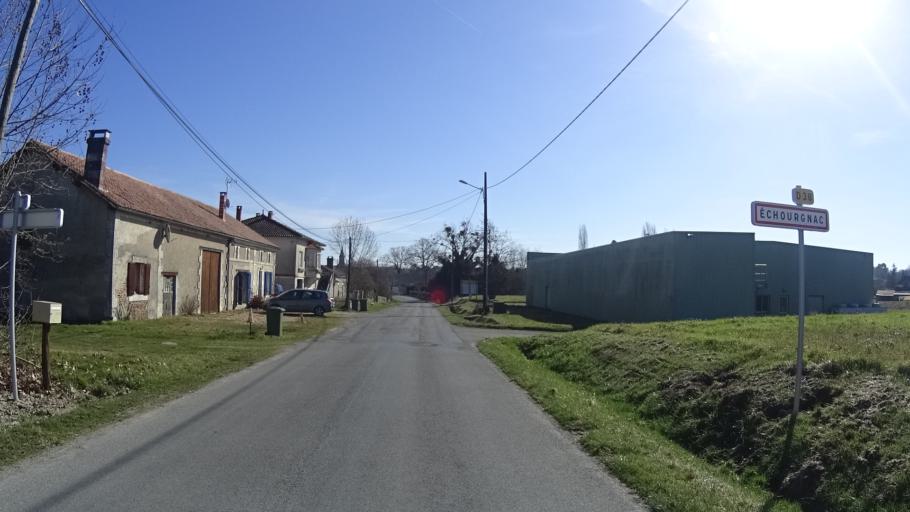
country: FR
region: Aquitaine
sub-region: Departement de la Dordogne
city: Saint-Aulaye
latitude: 45.1271
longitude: 0.2245
